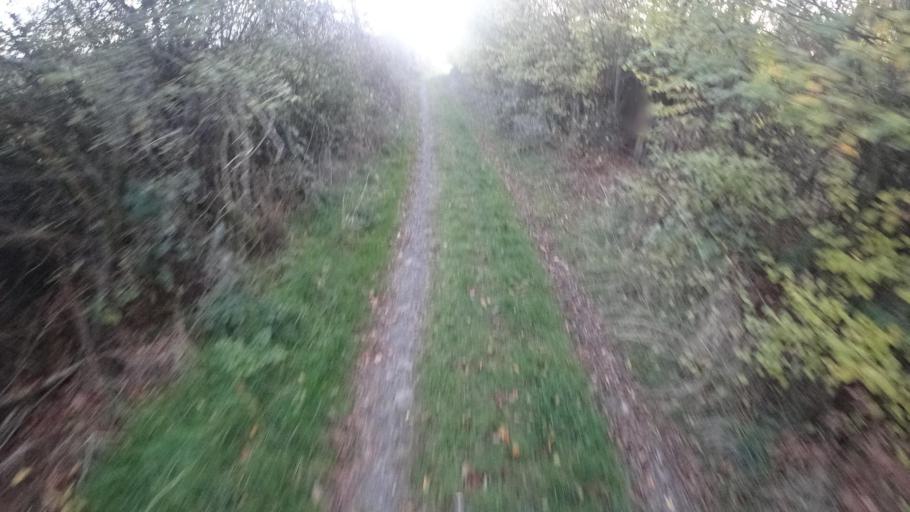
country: DE
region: Rheinland-Pfalz
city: Berg
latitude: 50.5298
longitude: 6.9489
